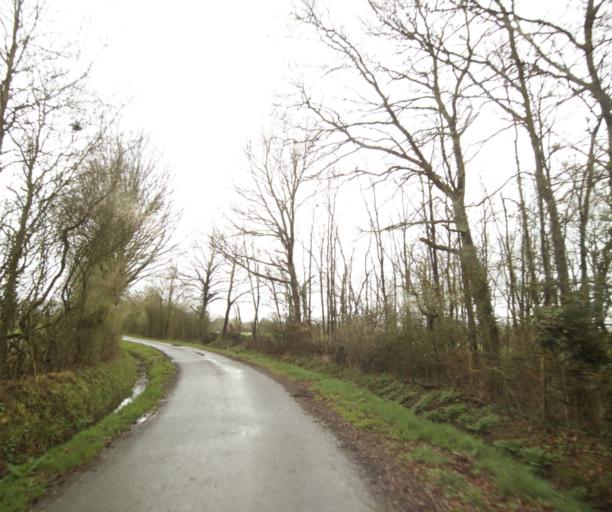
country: FR
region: Pays de la Loire
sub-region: Departement de la Loire-Atlantique
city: Bouvron
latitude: 47.4588
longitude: -1.8897
